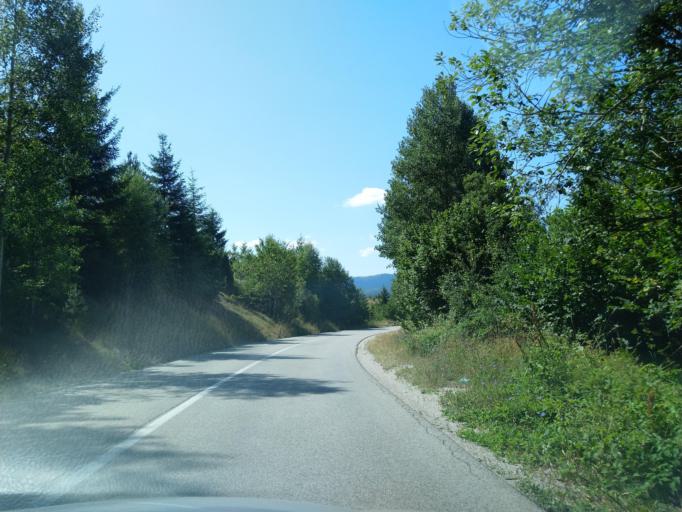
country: RS
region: Central Serbia
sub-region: Zlatiborski Okrug
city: Nova Varos
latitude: 43.3495
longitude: 19.8536
